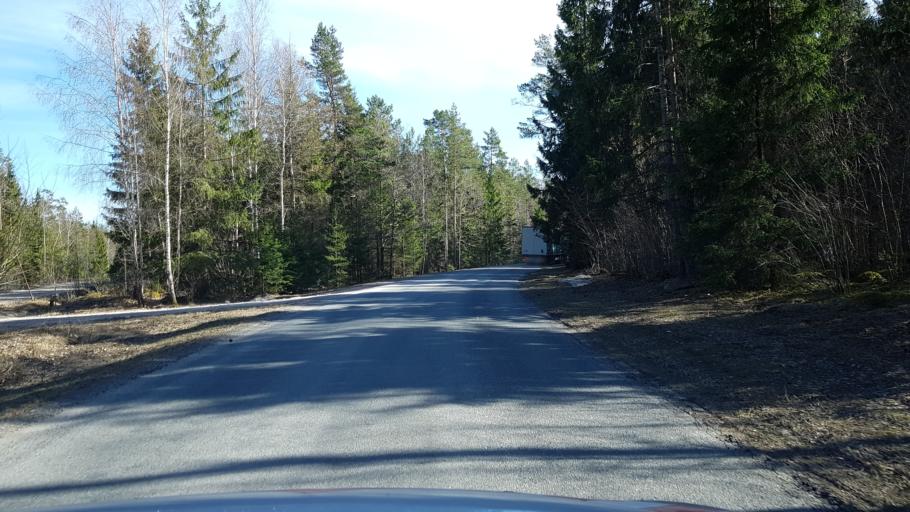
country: EE
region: Harju
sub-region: Nissi vald
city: Riisipere
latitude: 59.0863
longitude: 24.3535
